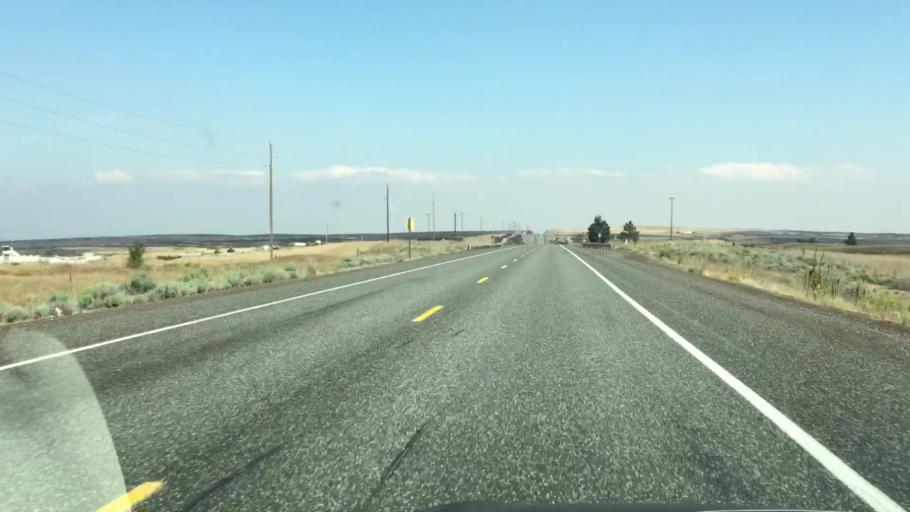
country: US
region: Oregon
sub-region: Wasco County
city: The Dalles
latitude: 45.3411
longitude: -121.1422
